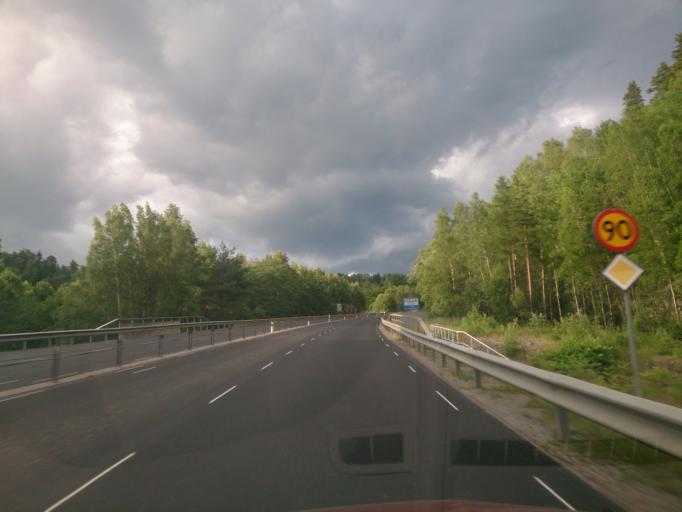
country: SE
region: OEstergoetland
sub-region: Norrkopings Kommun
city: Jursla
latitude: 58.6857
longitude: 16.1504
